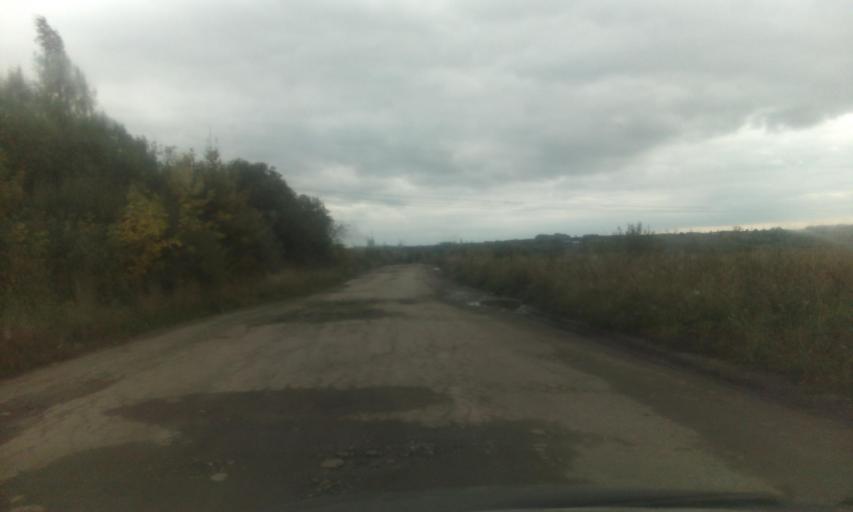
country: RU
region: Tula
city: Gritsovskiy
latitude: 54.1301
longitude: 38.1594
